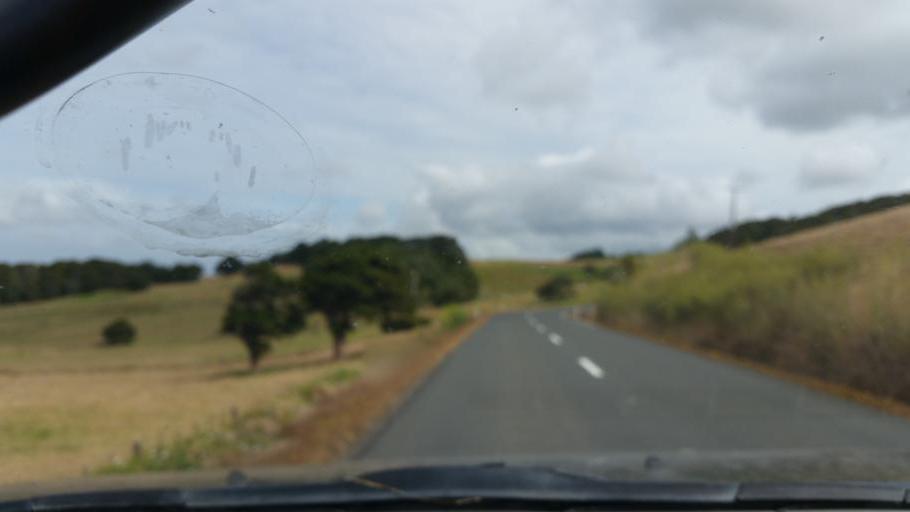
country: NZ
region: Northland
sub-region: Kaipara District
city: Dargaville
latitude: -35.9621
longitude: 173.9271
